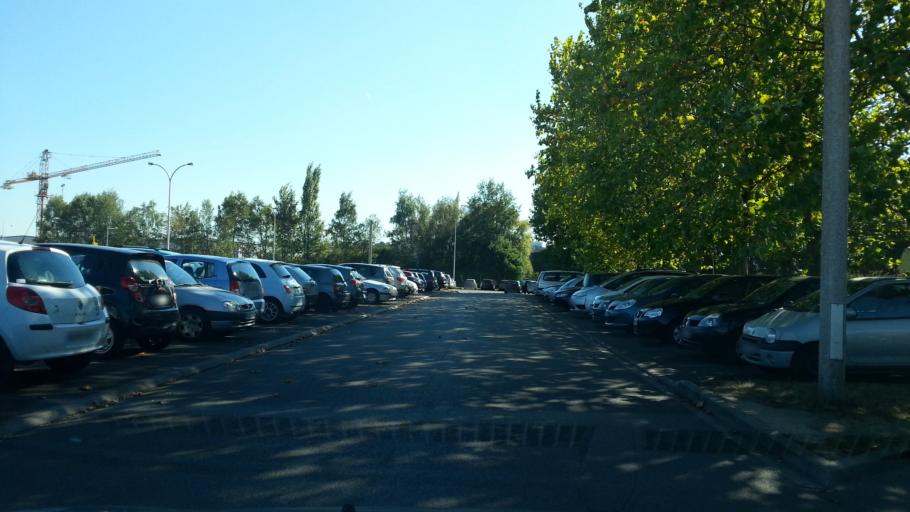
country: FR
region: Picardie
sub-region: Departement de l'Oise
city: Nogent-sur-Oise
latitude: 49.2656
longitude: 2.4621
